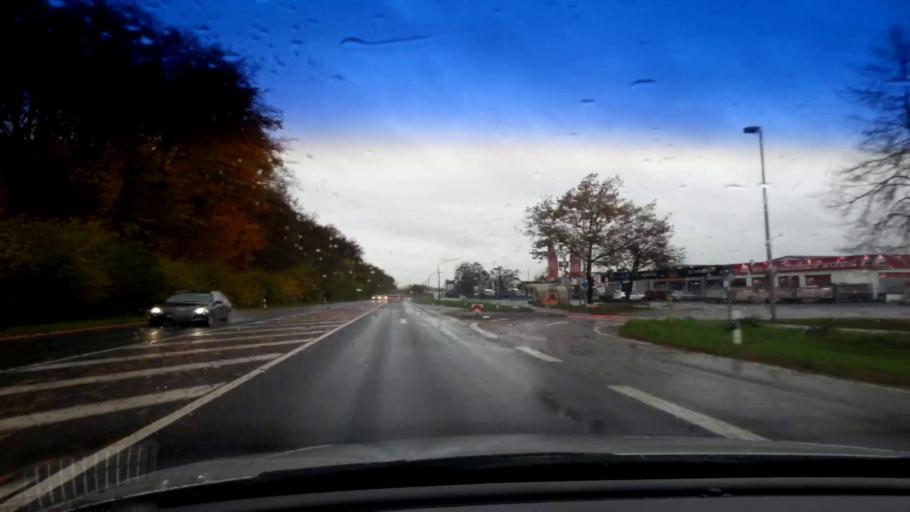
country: DE
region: Bavaria
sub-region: Upper Franconia
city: Oberhaid
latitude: 49.9177
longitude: 10.8069
